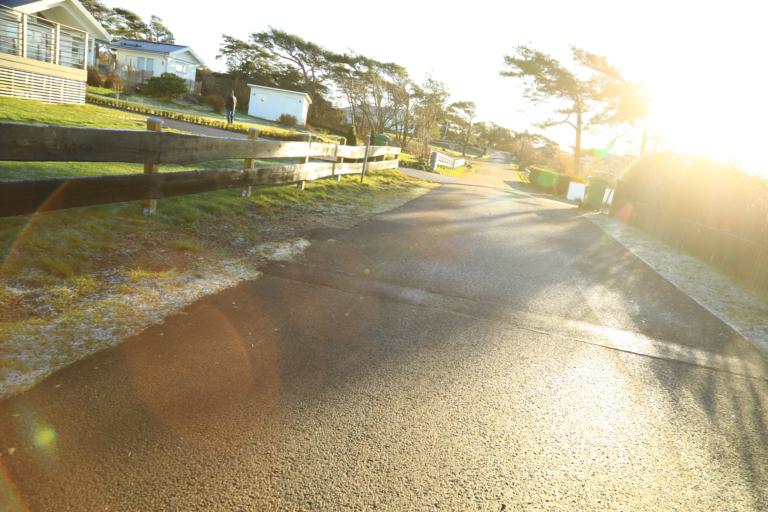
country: SE
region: Halland
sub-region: Varbergs Kommun
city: Varberg
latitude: 57.1887
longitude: 12.1637
